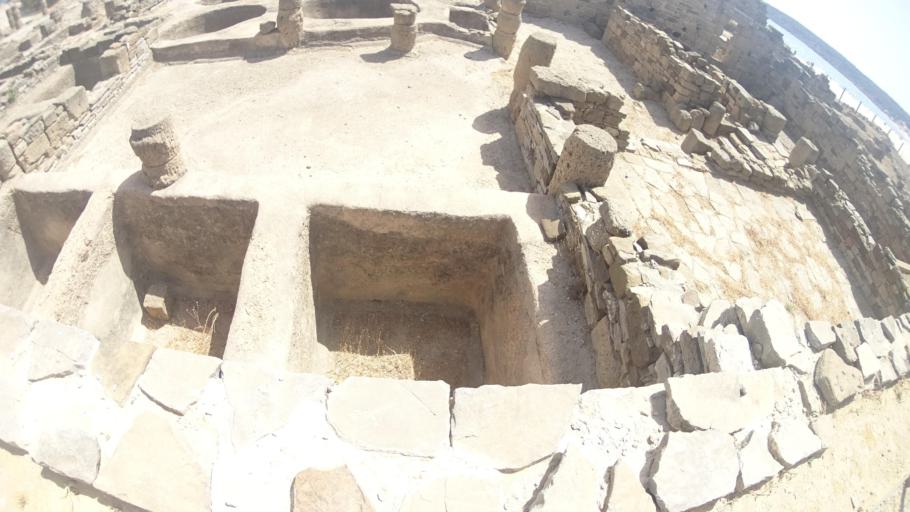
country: ES
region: Andalusia
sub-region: Provincia de Cadiz
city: Zahara de los Atunes
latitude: 36.0886
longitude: -5.7752
